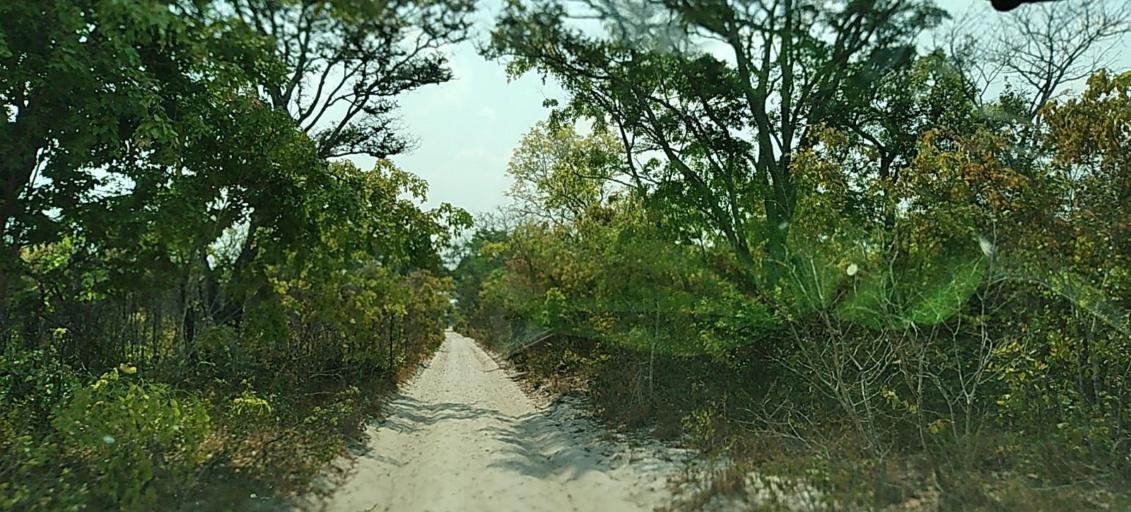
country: ZM
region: North-Western
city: Kabompo
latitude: -13.3886
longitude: 23.7773
